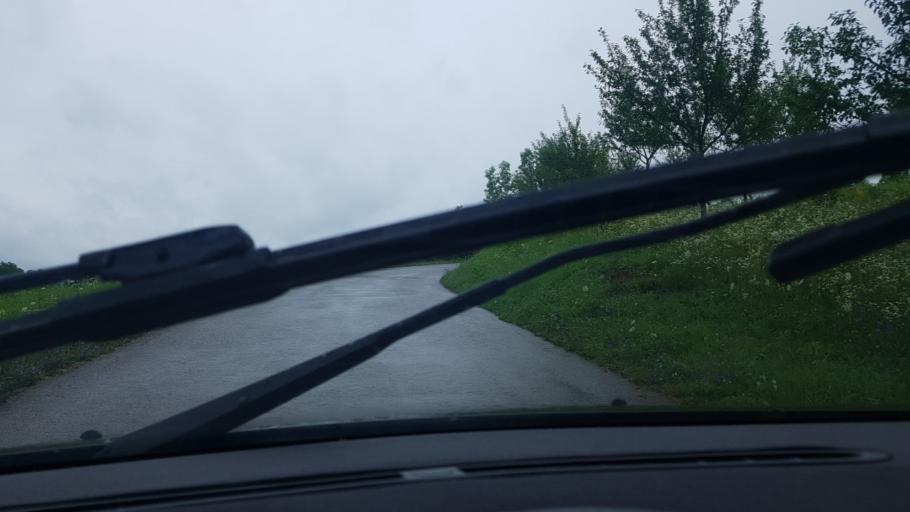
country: HR
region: Licko-Senjska
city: Jezerce
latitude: 44.9886
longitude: 15.6575
